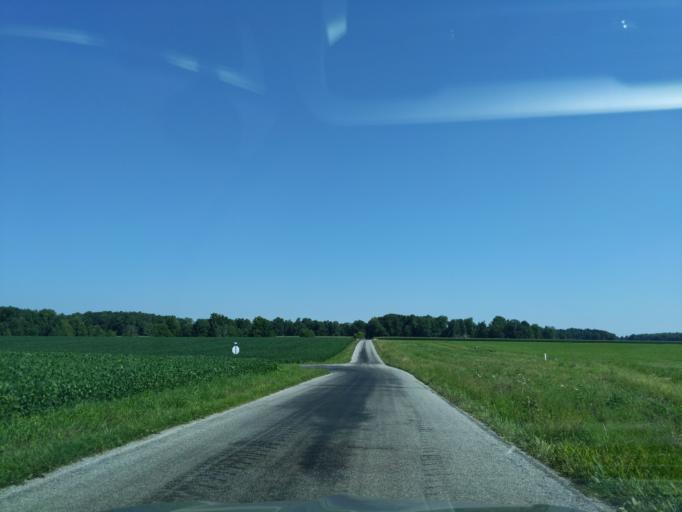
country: US
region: Indiana
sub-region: Ripley County
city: Osgood
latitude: 39.1108
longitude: -85.4321
